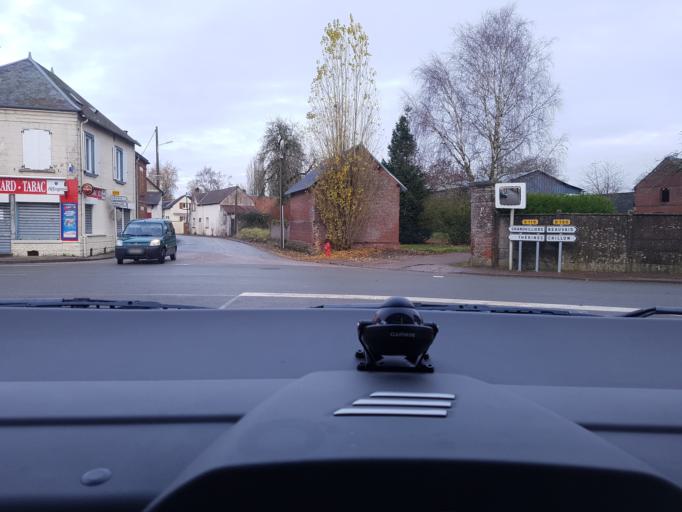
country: FR
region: Picardie
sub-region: Departement de l'Oise
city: Songeons
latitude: 49.5812
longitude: 1.8708
